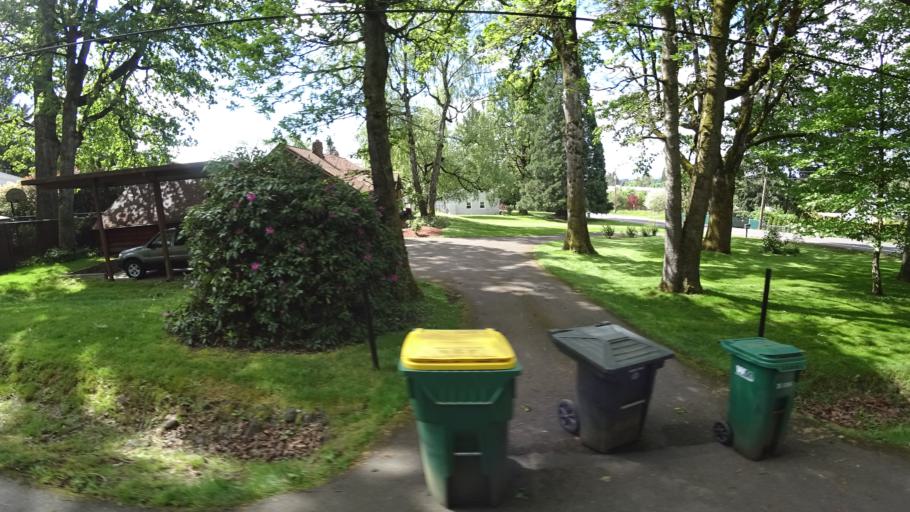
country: US
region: Oregon
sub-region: Washington County
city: Metzger
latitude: 45.4432
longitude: -122.7514
